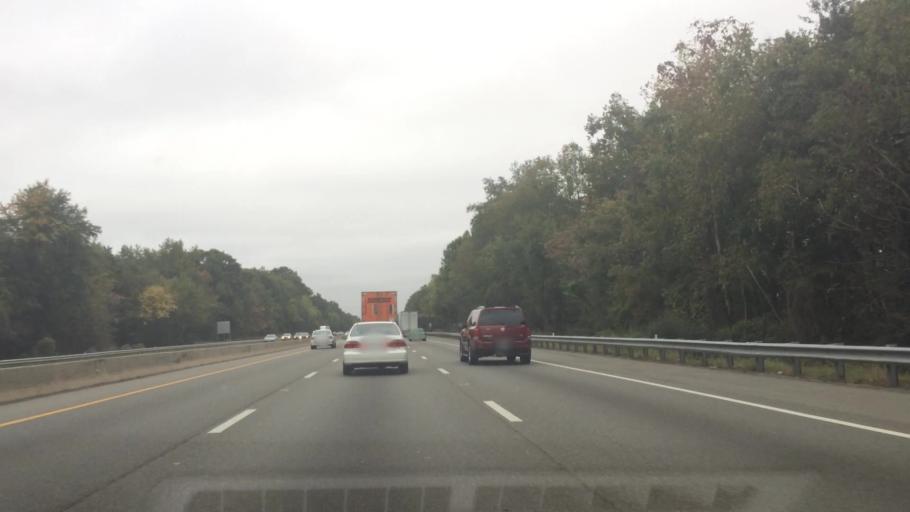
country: US
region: Virginia
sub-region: City of Colonial Heights
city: Colonial Heights
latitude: 37.2750
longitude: -77.3915
